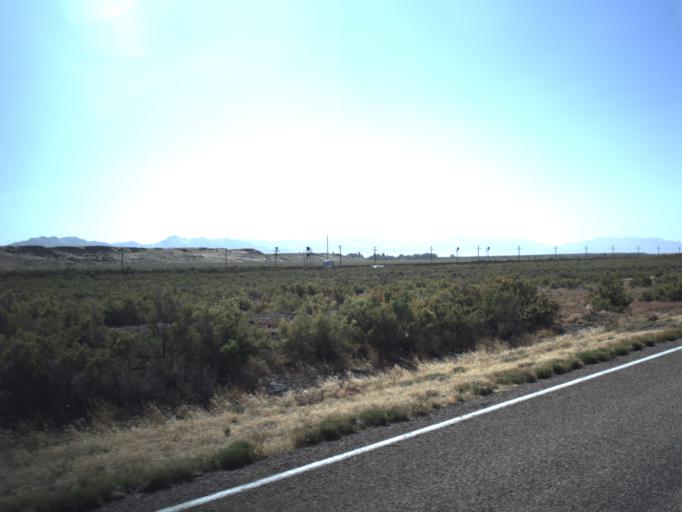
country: US
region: Utah
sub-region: Beaver County
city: Milford
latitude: 38.7292
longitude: -112.9666
